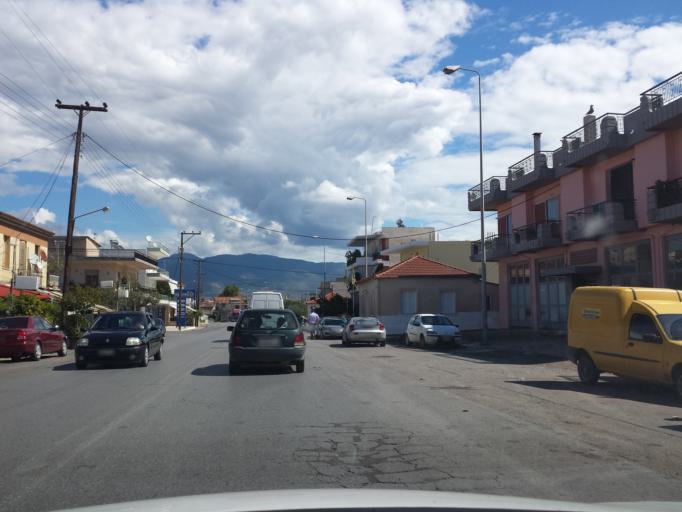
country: GR
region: Peloponnese
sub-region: Nomos Messinias
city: Messini
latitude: 37.0443
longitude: 22.0013
